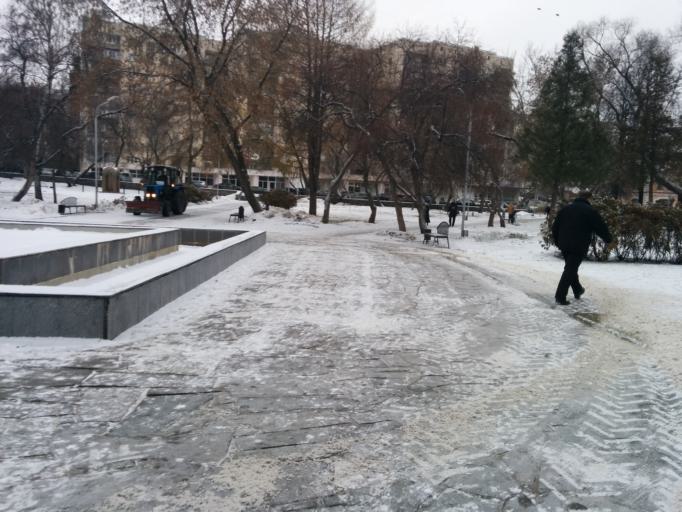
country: RU
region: Perm
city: Perm
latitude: 58.0125
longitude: 56.2320
